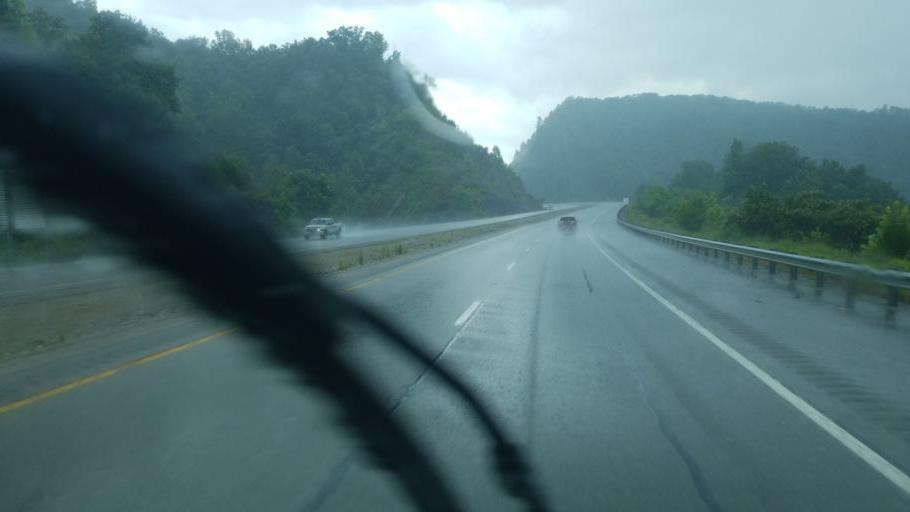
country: US
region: Kentucky
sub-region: Pike County
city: Pikeville
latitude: 37.5547
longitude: -82.4274
